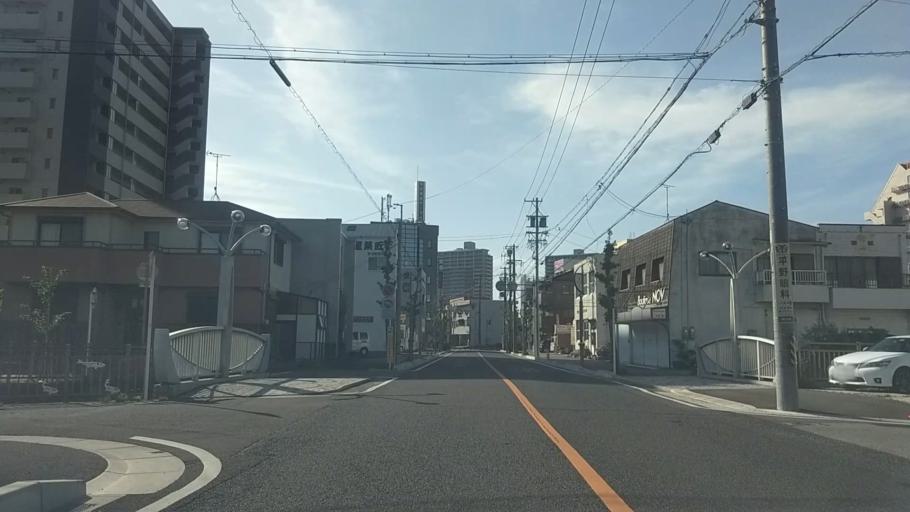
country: JP
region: Aichi
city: Anjo
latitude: 34.9585
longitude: 137.0893
